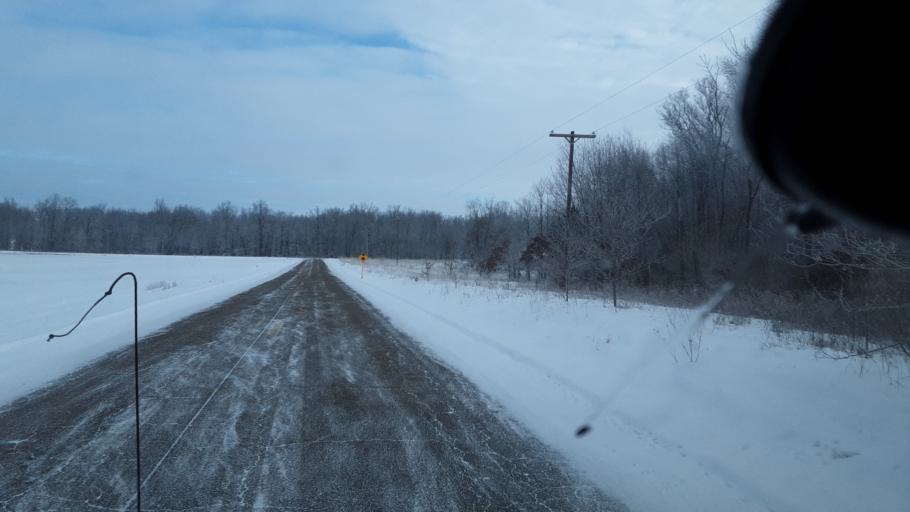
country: US
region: Michigan
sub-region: Ingham County
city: Leslie
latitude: 42.4006
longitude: -84.4857
